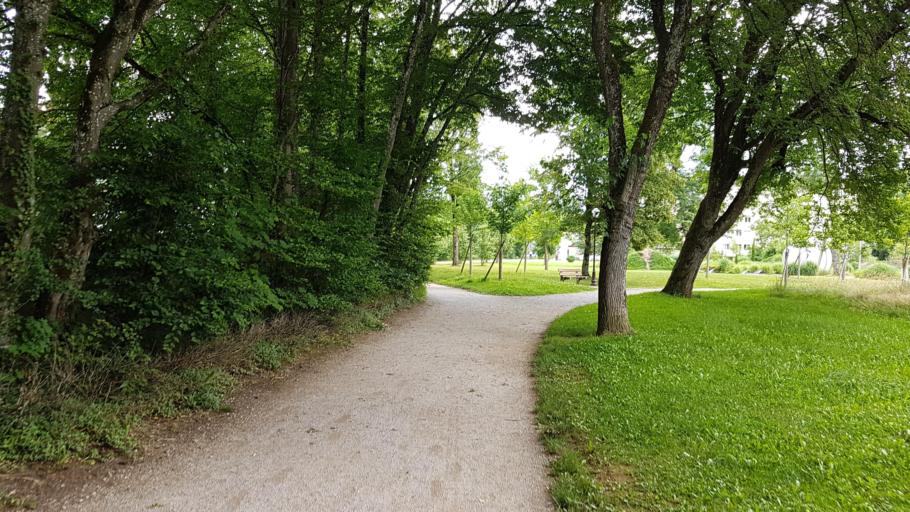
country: FR
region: Franche-Comte
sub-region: Departement du Jura
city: Lons-le-Saunier
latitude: 46.6713
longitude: 5.5667
